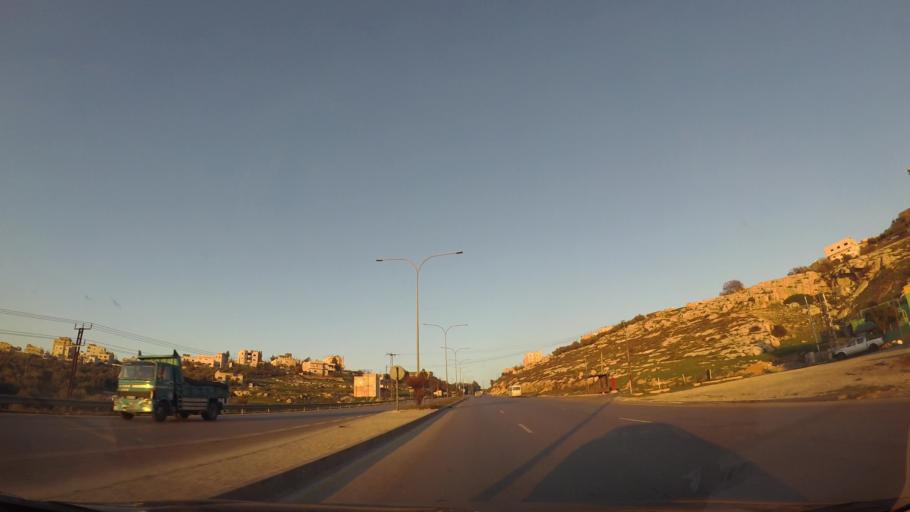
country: JO
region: Amman
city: Umm as Summaq
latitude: 31.8610
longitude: 35.8129
